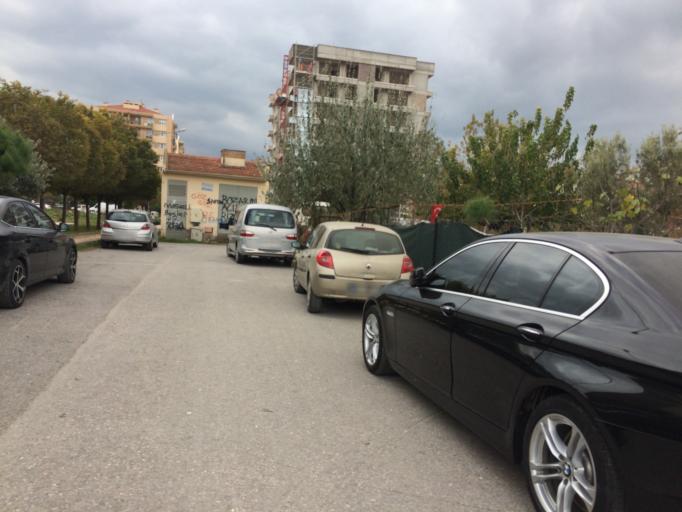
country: TR
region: Izmir
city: Karsiyaka
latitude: 38.4850
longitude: 27.0605
